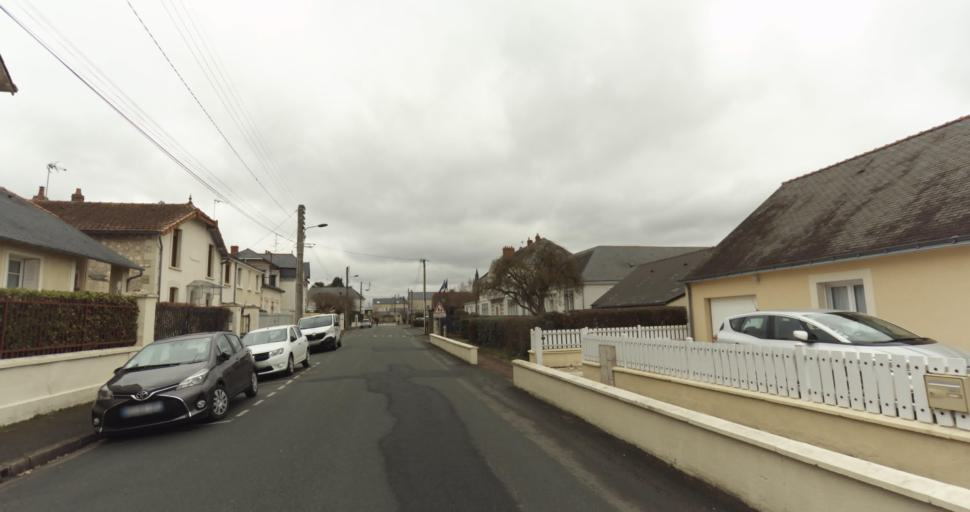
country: FR
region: Pays de la Loire
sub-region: Departement de Maine-et-Loire
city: Saumur
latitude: 47.2436
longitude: -0.0942
